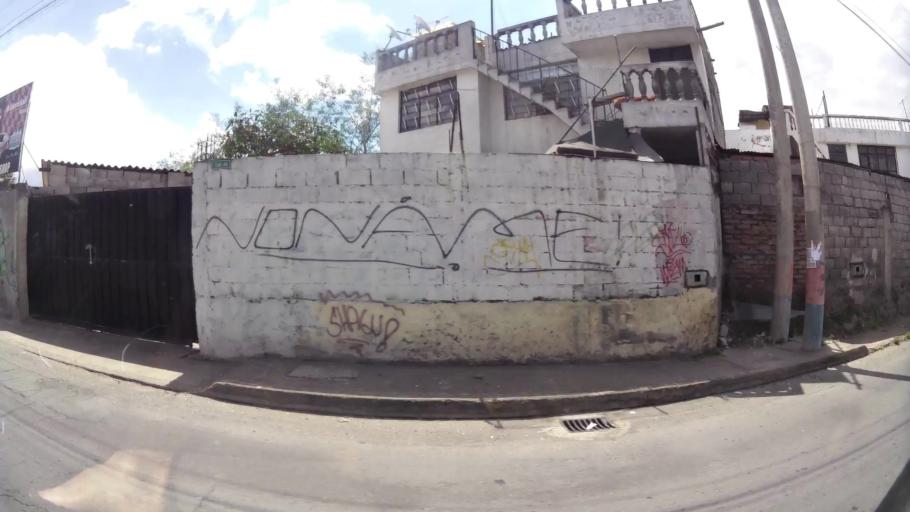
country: EC
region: Pichincha
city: Quito
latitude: -0.1048
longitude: -78.4240
